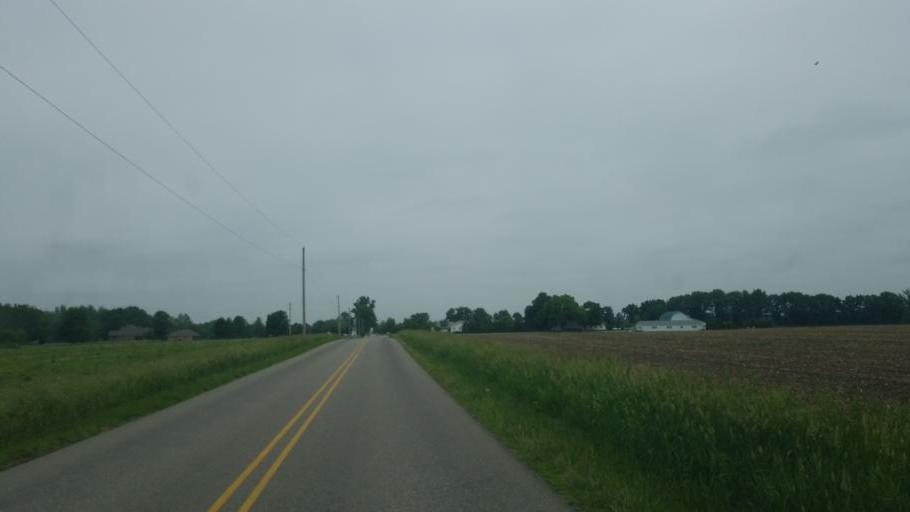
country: US
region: Indiana
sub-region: Elkhart County
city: Nappanee
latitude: 41.4606
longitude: -86.0207
